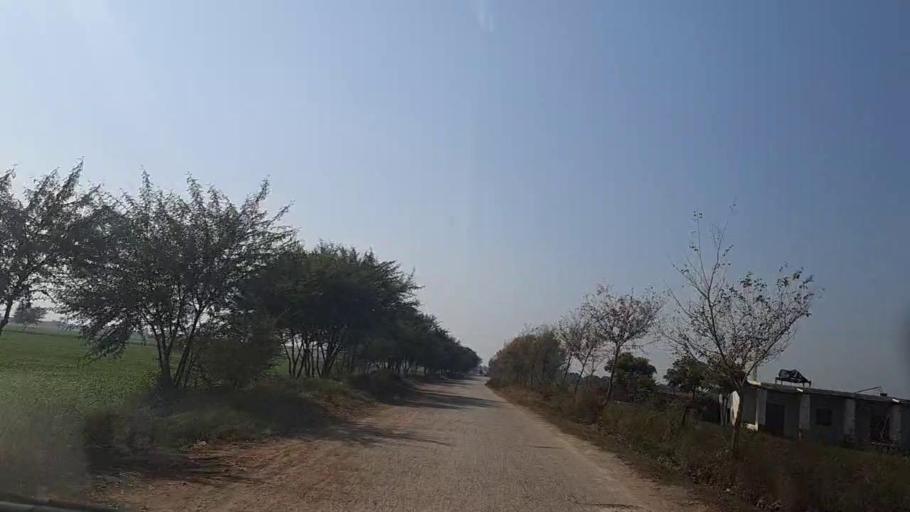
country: PK
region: Sindh
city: Sakrand
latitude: 26.0238
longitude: 68.3675
